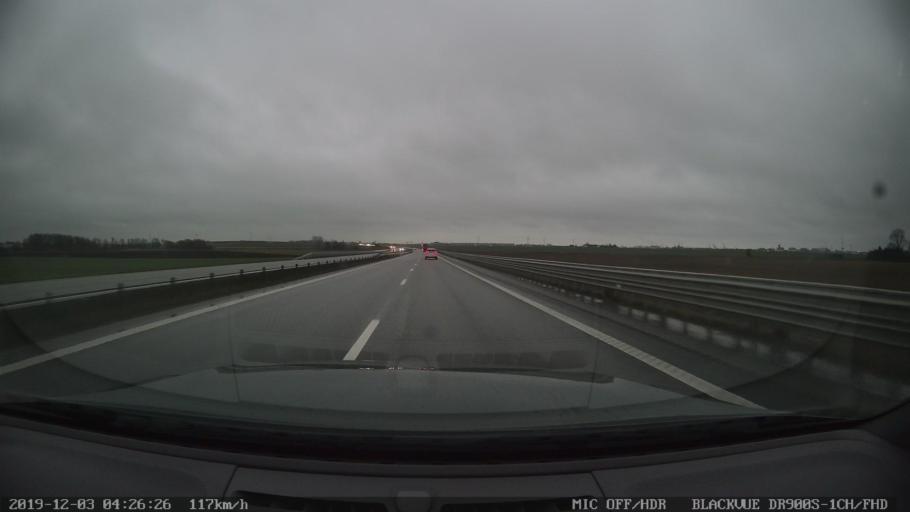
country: SE
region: Skane
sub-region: Landskrona
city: Landskrona
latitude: 55.8962
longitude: 12.8672
